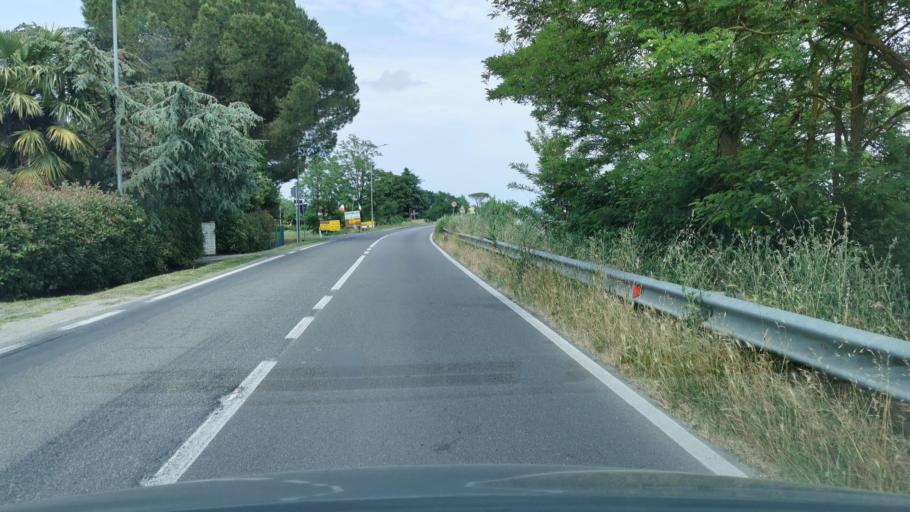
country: IT
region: Emilia-Romagna
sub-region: Provincia di Ravenna
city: Sant'Alberto
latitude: 44.5463
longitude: 12.2116
